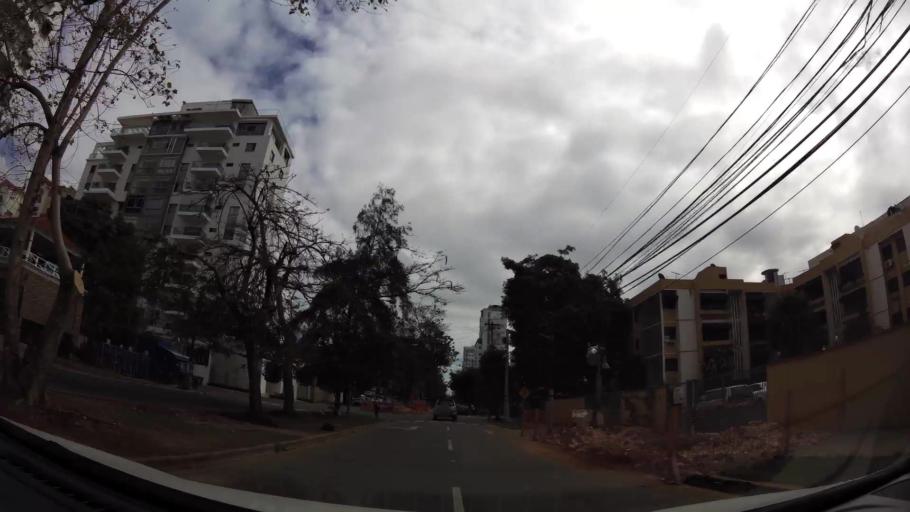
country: DO
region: Nacional
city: Bella Vista
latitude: 18.4494
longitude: -69.9507
